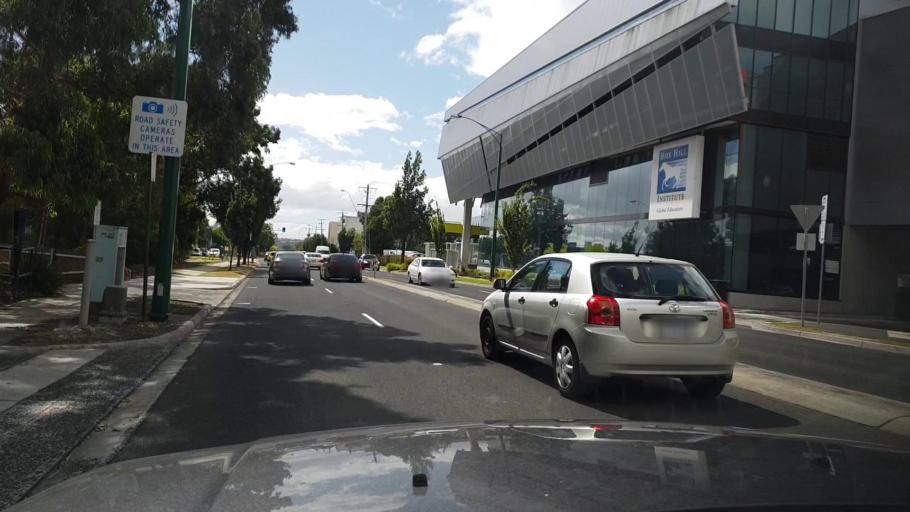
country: AU
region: Victoria
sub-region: Whitehorse
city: Box Hill
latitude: -37.8153
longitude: 145.1153
